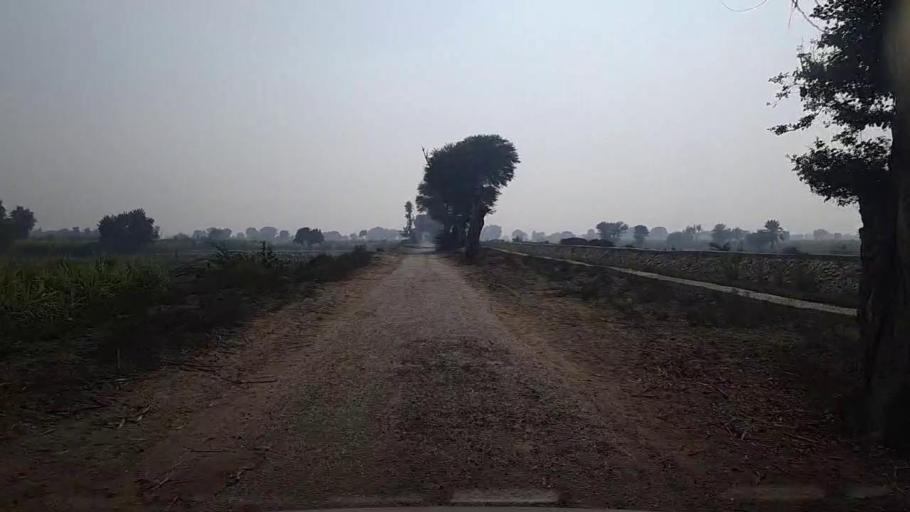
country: PK
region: Sindh
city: Setharja Old
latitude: 27.1179
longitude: 68.5100
